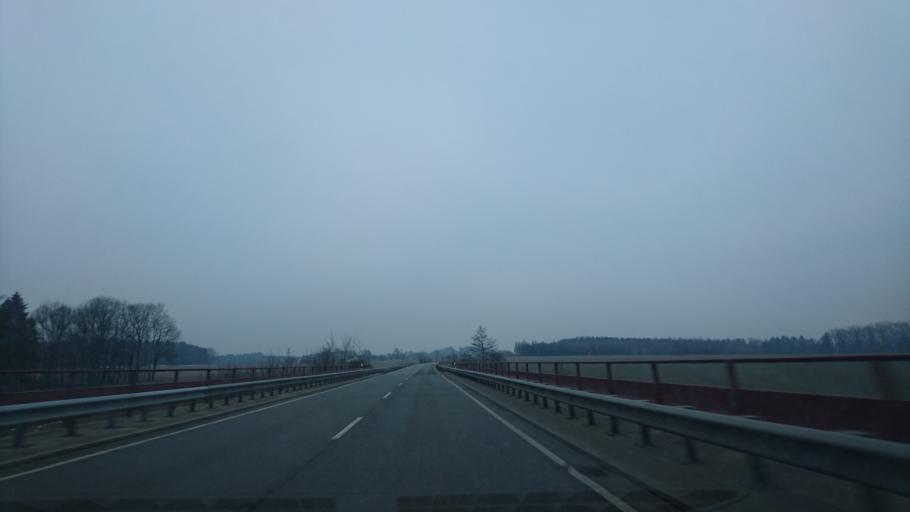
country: DE
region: Bavaria
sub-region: Lower Bavaria
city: Bad Griesbach
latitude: 48.4354
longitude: 13.1742
